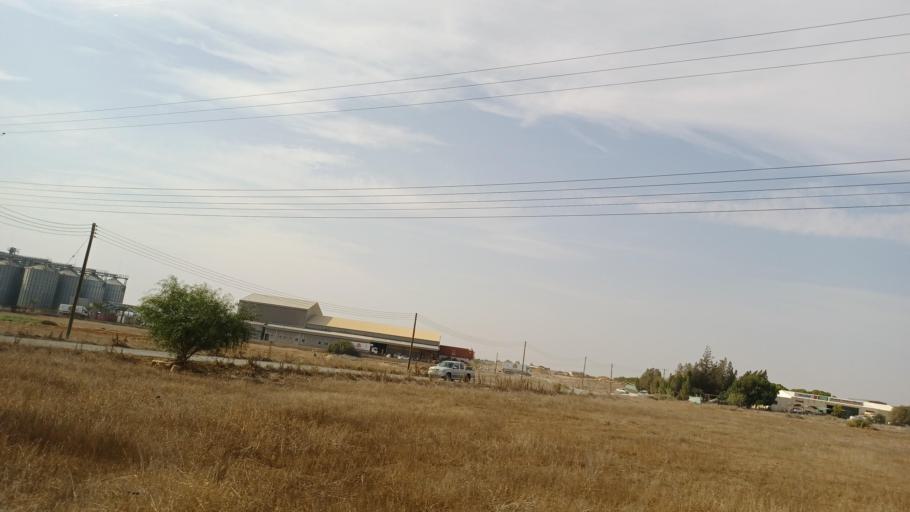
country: CY
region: Ammochostos
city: Frenaros
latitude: 35.0293
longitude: 33.9131
